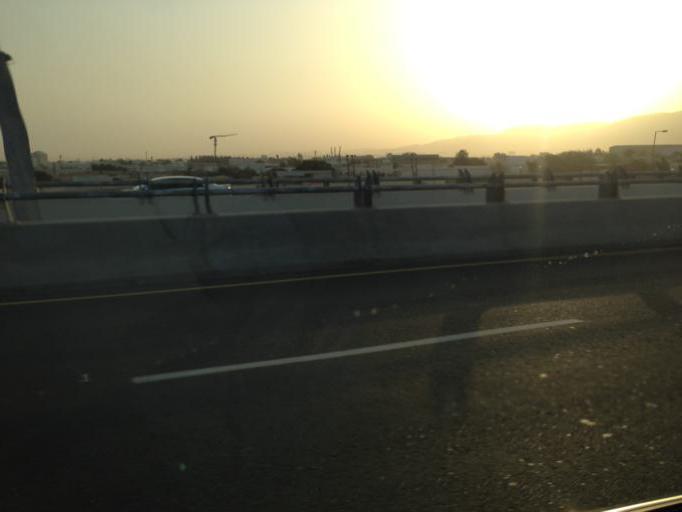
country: OM
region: Muhafazat Masqat
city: Bawshar
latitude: 23.5700
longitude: 58.3334
